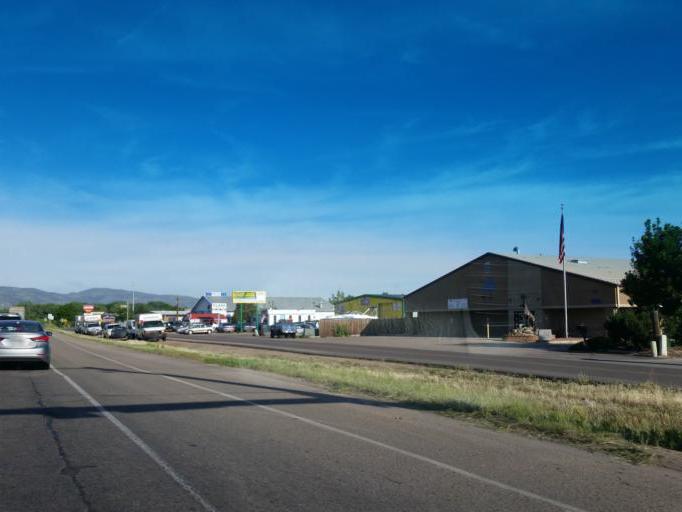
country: US
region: Colorado
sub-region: Larimer County
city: Fort Collins
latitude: 40.5814
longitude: -105.0504
